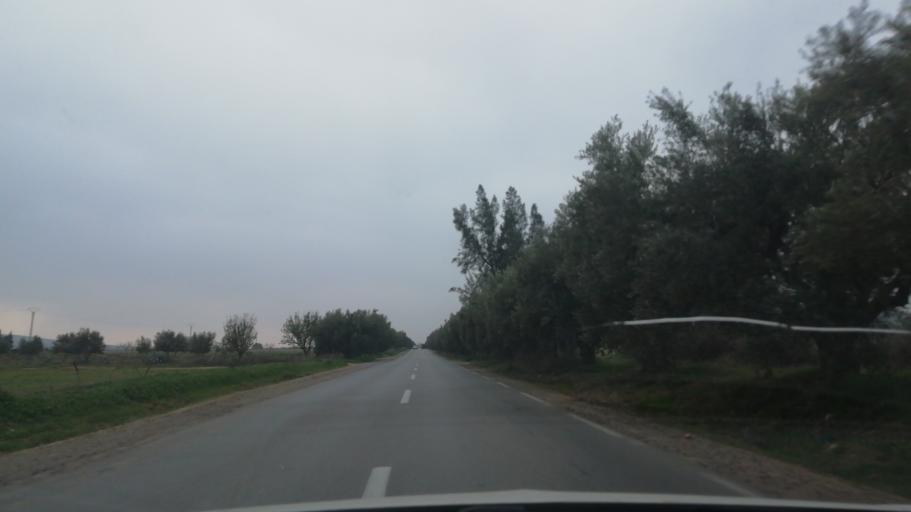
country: DZ
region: Sidi Bel Abbes
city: Sfizef
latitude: 35.2619
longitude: -0.1742
